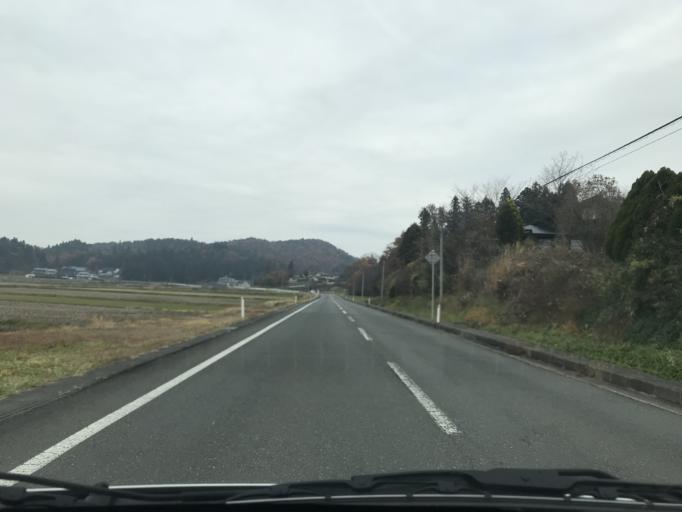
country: JP
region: Iwate
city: Mizusawa
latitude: 39.1748
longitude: 141.2154
